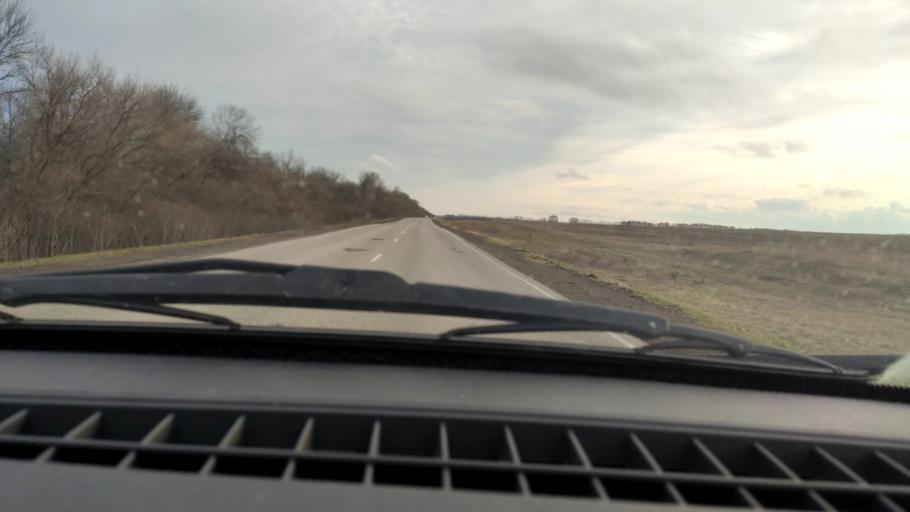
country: RU
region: Bashkortostan
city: Chishmy
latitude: 54.4773
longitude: 55.2666
